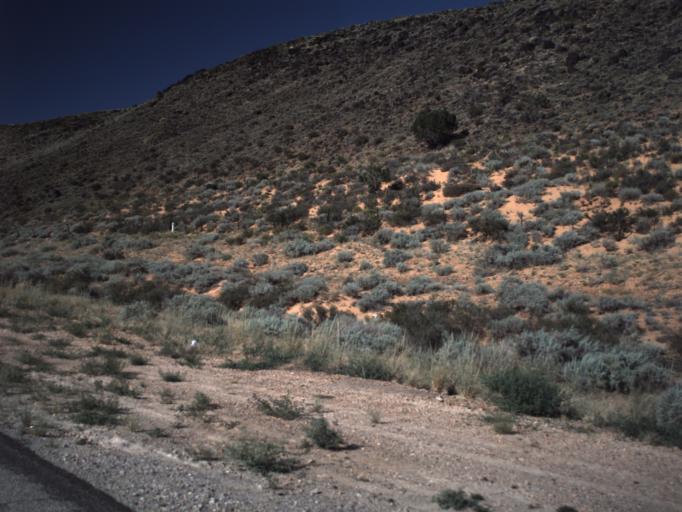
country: US
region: Utah
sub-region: Washington County
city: Toquerville
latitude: 37.2691
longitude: -113.2961
